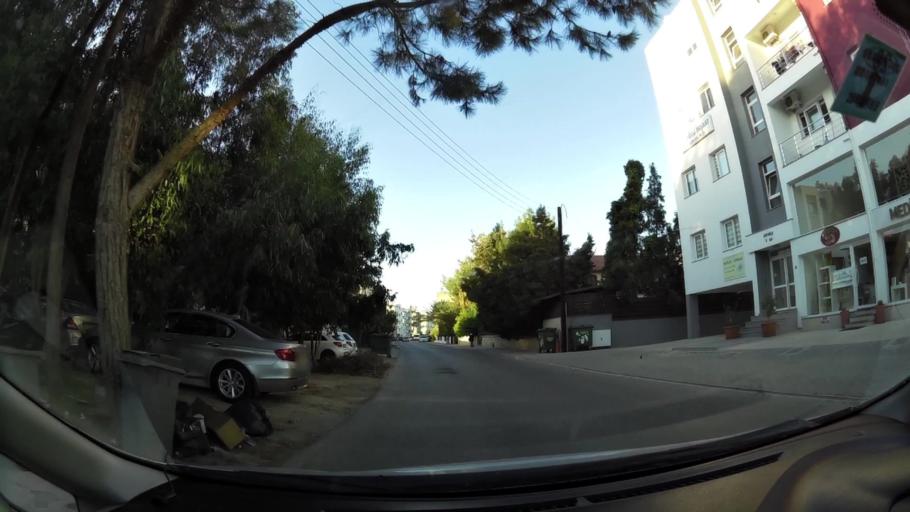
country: CY
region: Lefkosia
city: Nicosia
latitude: 35.2057
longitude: 33.3183
